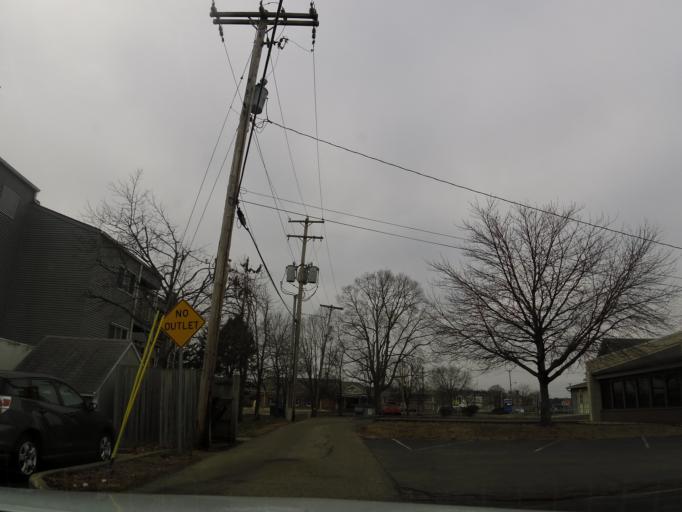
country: US
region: Indiana
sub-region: Bartholomew County
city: Columbus
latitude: 39.2010
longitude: -85.9160
